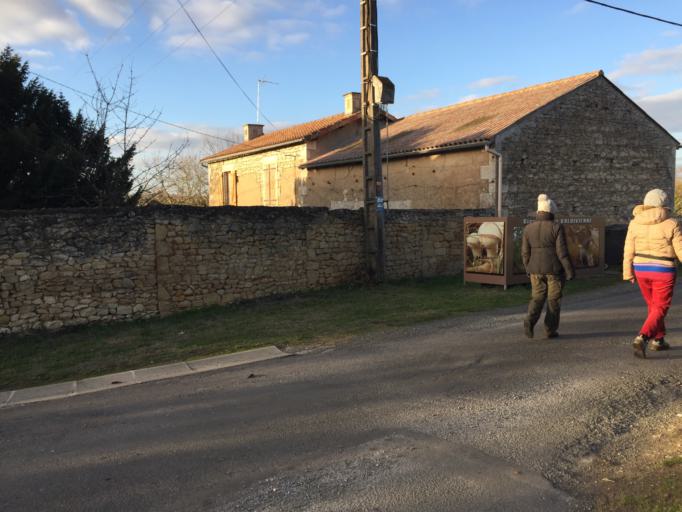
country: FR
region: Poitou-Charentes
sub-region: Departement de la Vienne
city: Chauvigny
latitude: 46.5187
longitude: 0.6463
